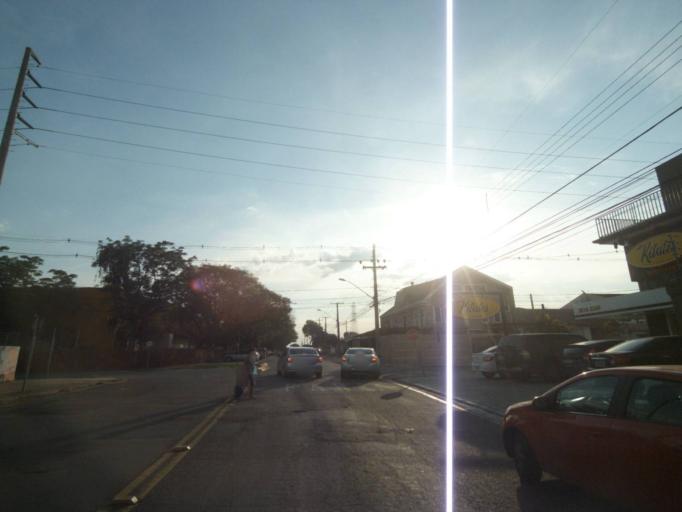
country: BR
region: Parana
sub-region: Curitiba
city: Curitiba
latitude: -25.4626
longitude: -49.3116
